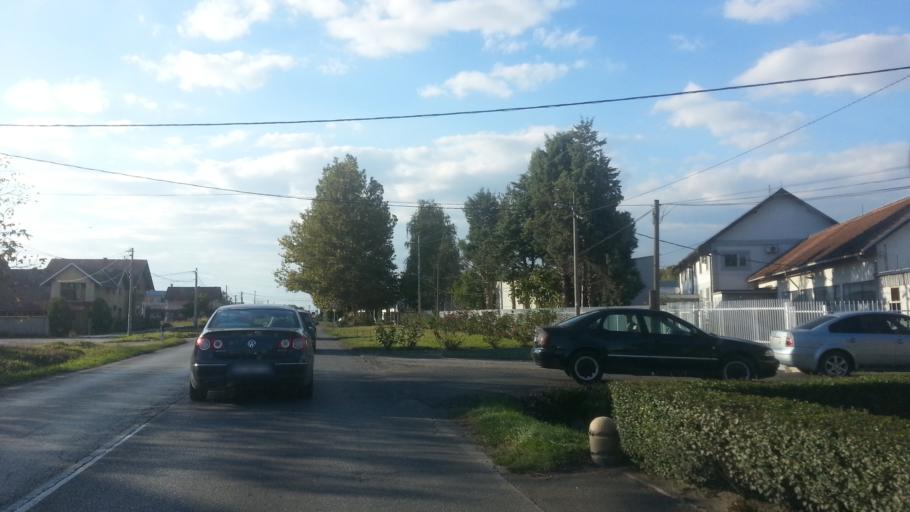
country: RS
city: Novi Banovci
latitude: 44.9135
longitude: 20.2613
